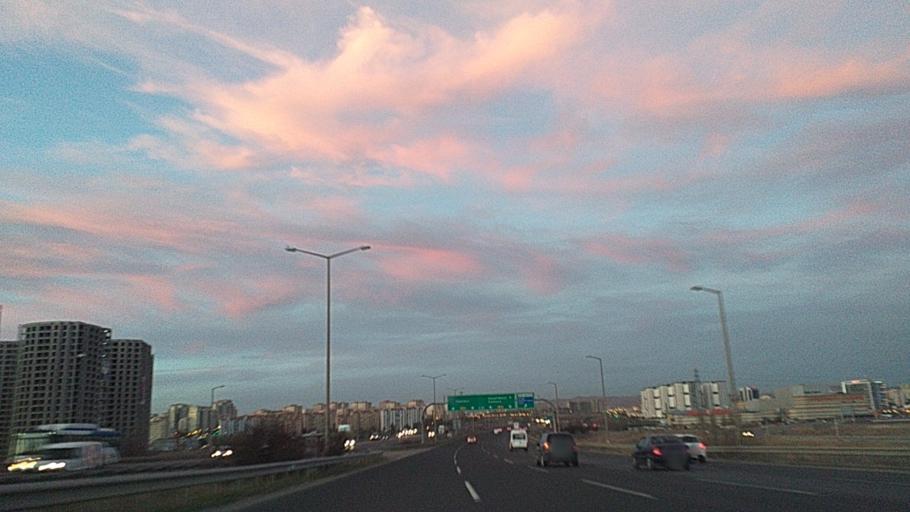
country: TR
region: Ankara
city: Etimesgut
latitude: 39.9601
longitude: 32.6256
